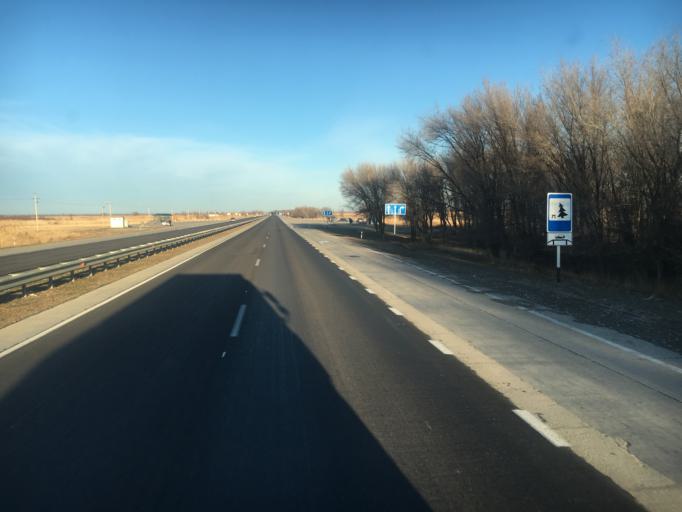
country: KZ
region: Ongtustik Qazaqstan
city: Bayaldyr
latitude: 43.0882
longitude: 68.6431
